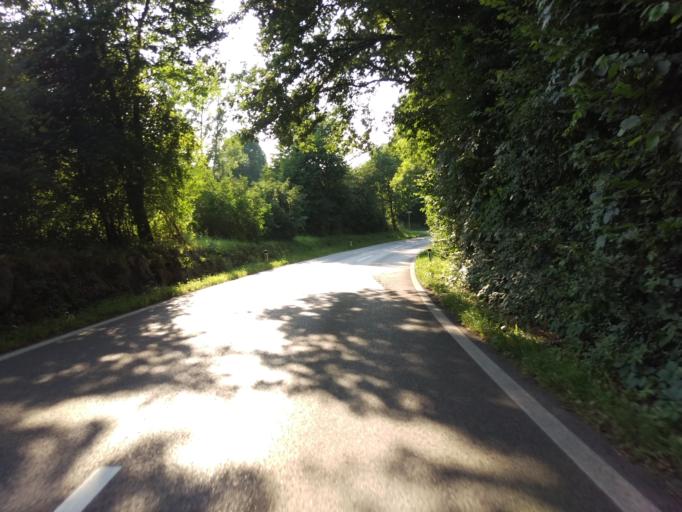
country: AT
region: Styria
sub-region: Politischer Bezirk Graz-Umgebung
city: Thal
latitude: 47.0693
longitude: 15.3643
